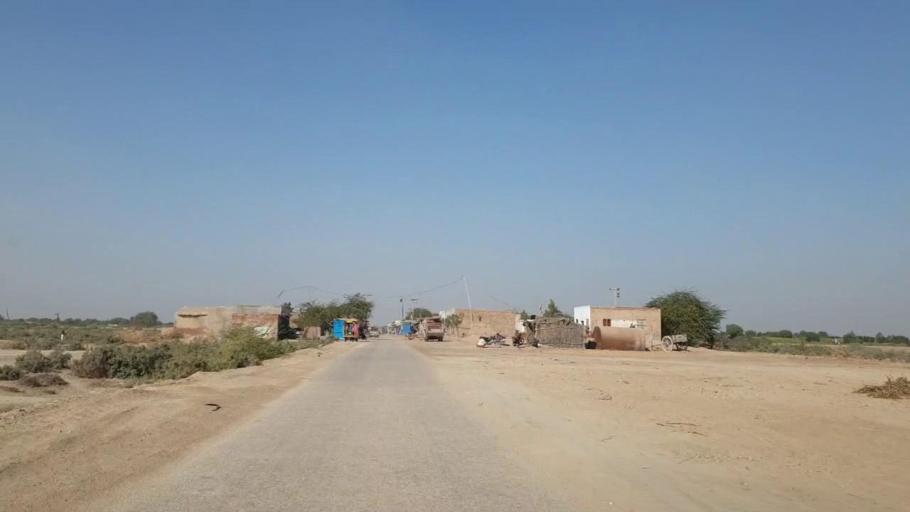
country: PK
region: Sindh
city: Digri
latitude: 25.0312
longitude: 69.1051
